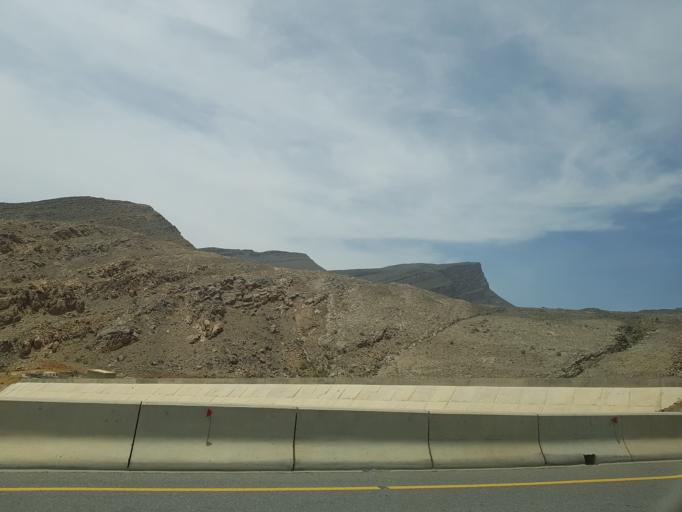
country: OM
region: Muhafazat ad Dakhiliyah
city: Izki
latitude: 22.9630
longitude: 57.6833
